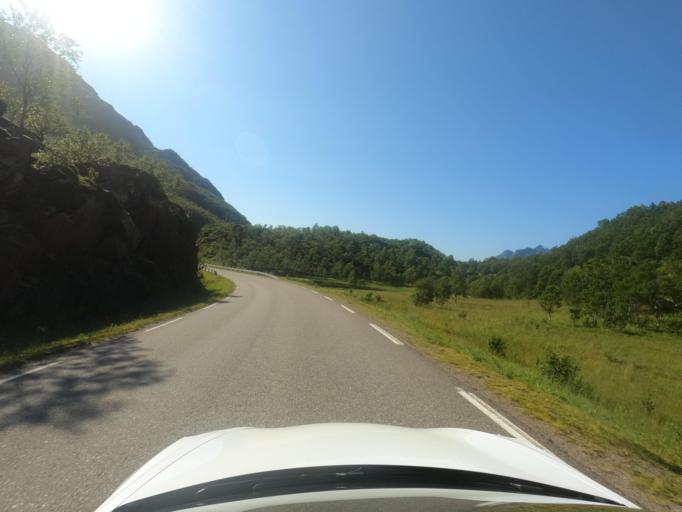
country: NO
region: Nordland
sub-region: Hadsel
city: Stokmarknes
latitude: 68.4533
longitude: 15.2043
